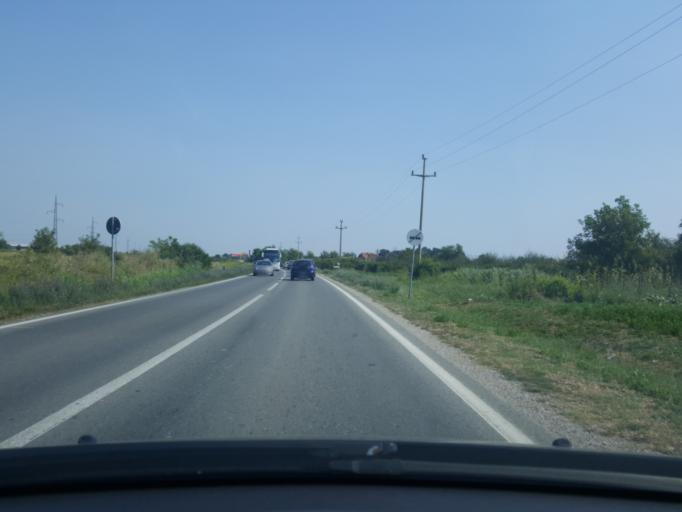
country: RS
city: Majur
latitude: 44.7669
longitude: 19.6309
